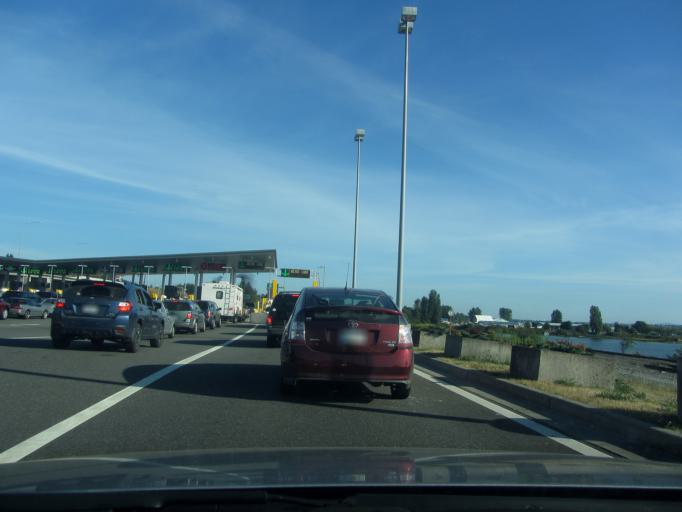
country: US
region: Washington
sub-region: Whatcom County
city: Blaine
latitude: 49.0008
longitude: -122.7561
